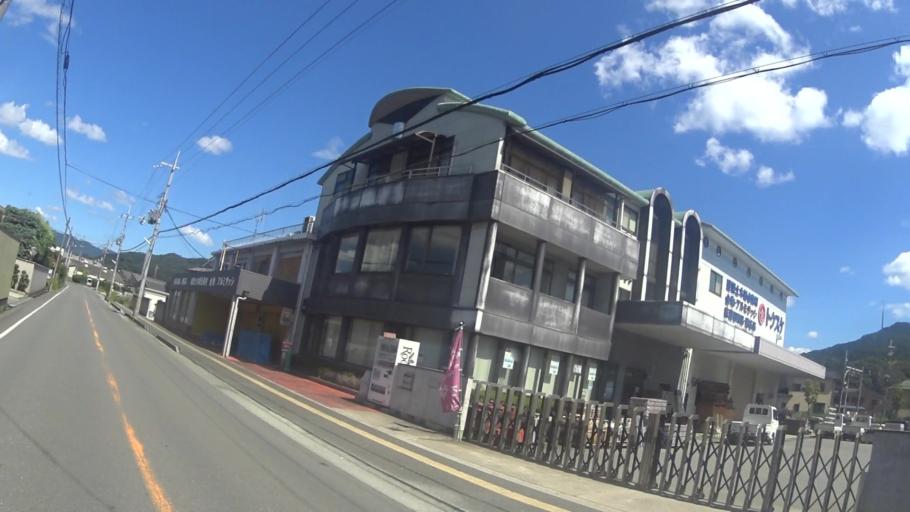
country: JP
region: Nara
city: Nara-shi
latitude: 34.7554
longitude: 135.8714
